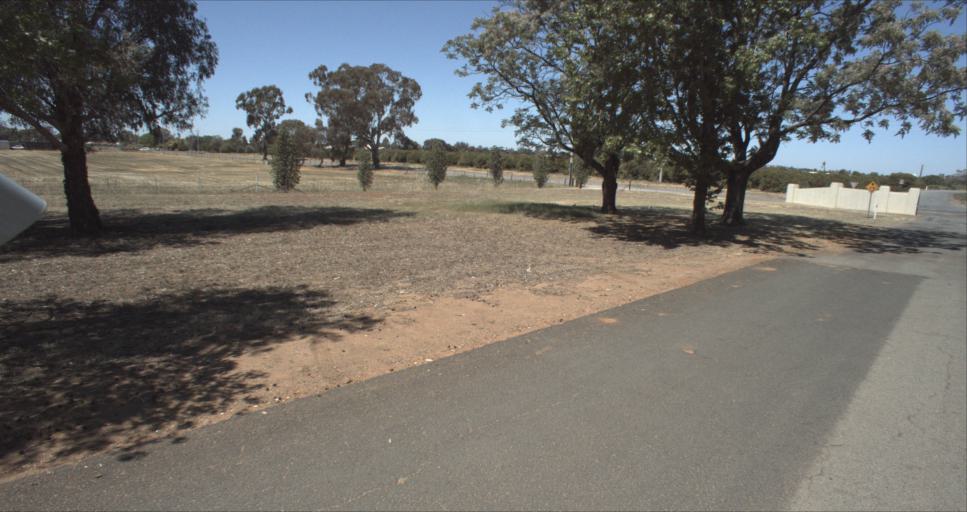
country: AU
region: New South Wales
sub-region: Leeton
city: Leeton
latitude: -34.5326
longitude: 146.3990
